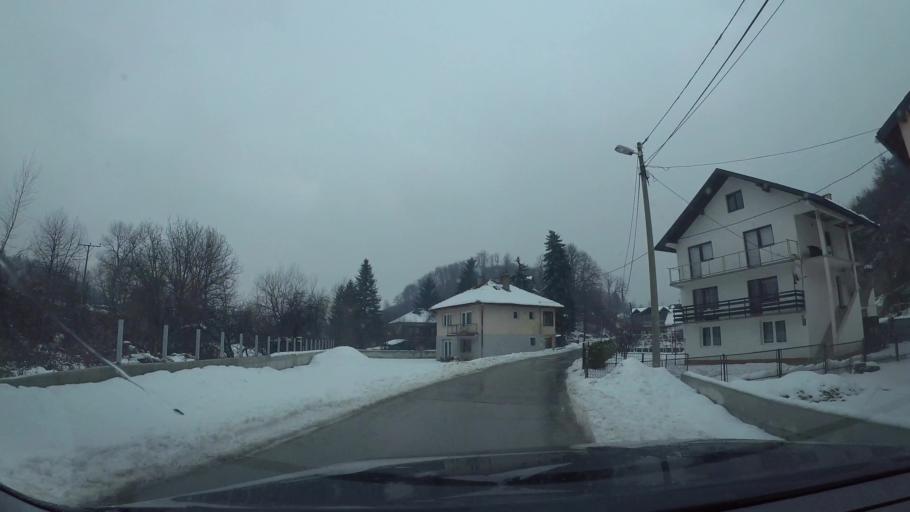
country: BA
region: Federation of Bosnia and Herzegovina
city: Hadzici
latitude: 43.8414
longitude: 18.2593
